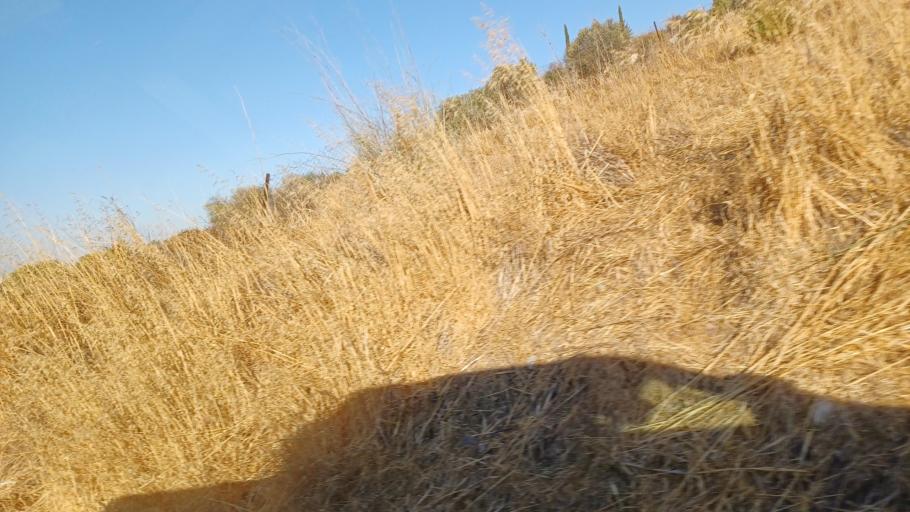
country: CY
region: Pafos
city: Mesogi
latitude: 34.9177
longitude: 32.5335
